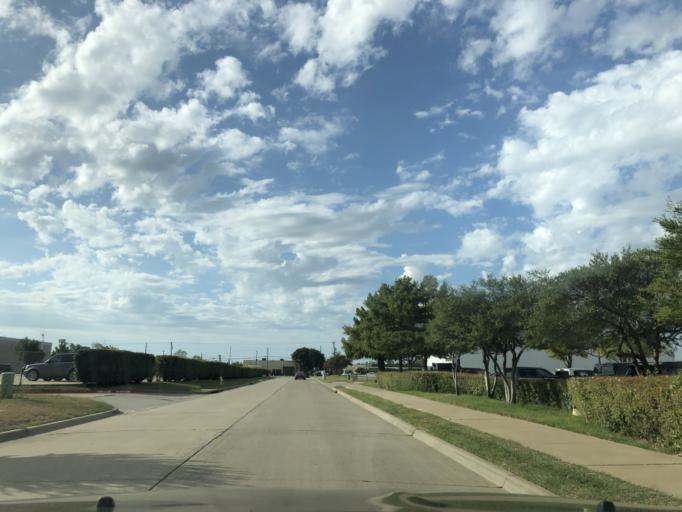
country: US
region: Texas
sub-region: Dallas County
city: Garland
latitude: 32.8809
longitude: -96.6682
